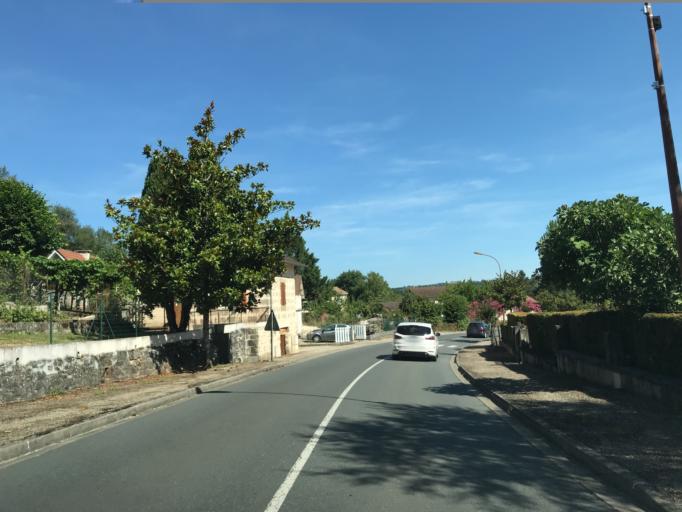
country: FR
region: Limousin
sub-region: Departement de la Correze
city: Larche
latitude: 45.1186
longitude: 1.4102
